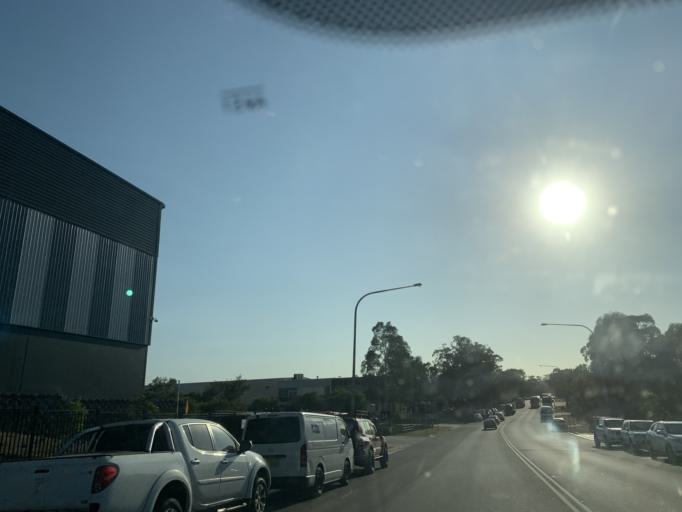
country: AU
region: New South Wales
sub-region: Blacktown
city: Doonside
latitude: -33.7977
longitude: 150.8821
